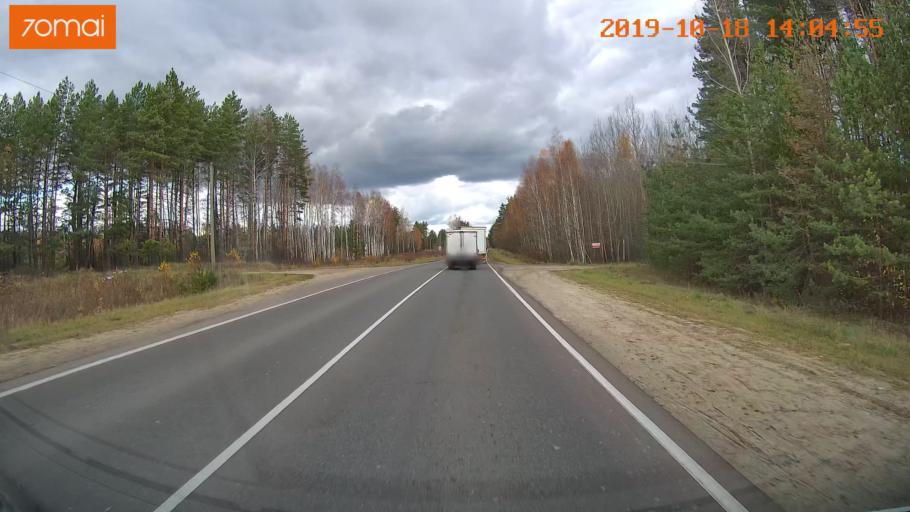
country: RU
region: Rjazan
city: Spas-Klepiki
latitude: 55.1306
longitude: 40.1344
